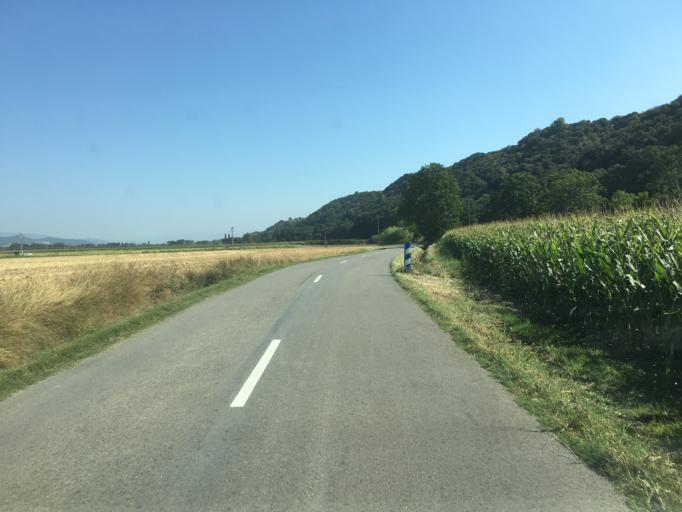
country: FR
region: Provence-Alpes-Cote d'Azur
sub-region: Departement des Alpes-de-Haute-Provence
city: Manosque
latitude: 43.8086
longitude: 5.8436
